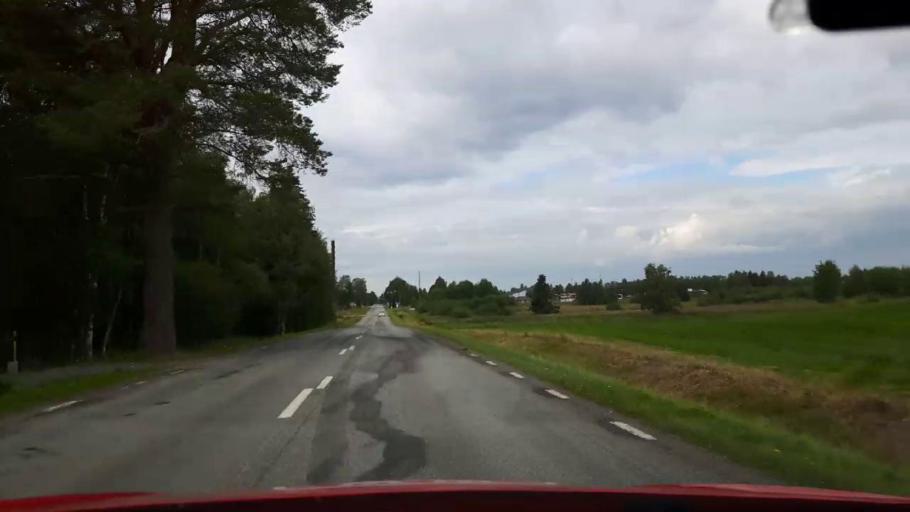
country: SE
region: Jaemtland
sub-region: Stroemsunds Kommun
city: Stroemsund
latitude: 63.8452
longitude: 15.5778
